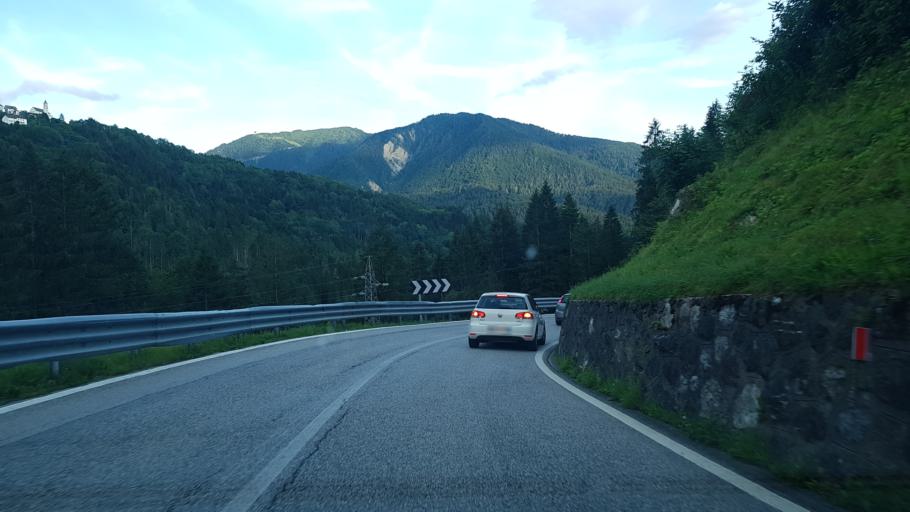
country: IT
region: Friuli Venezia Giulia
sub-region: Provincia di Udine
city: Comeglians
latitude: 46.5347
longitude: 12.8660
